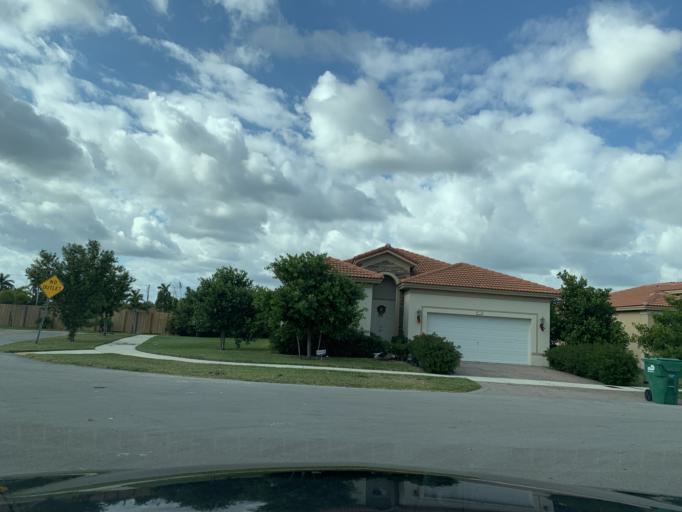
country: US
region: Florida
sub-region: Miami-Dade County
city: Naranja
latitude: 25.5093
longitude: -80.4108
